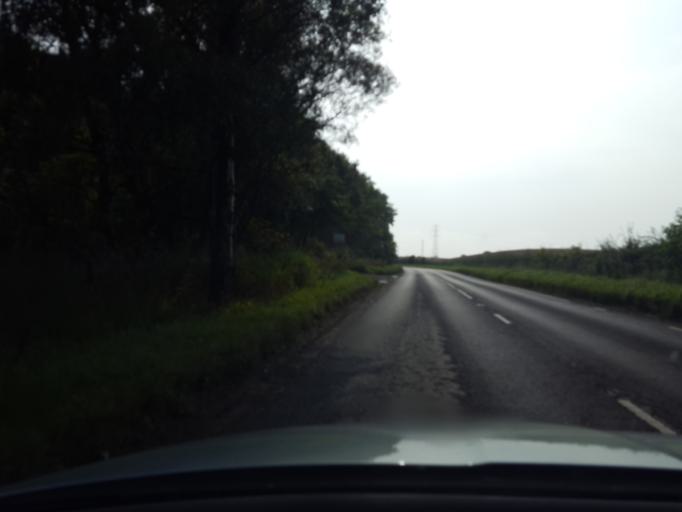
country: GB
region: Scotland
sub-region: Fife
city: Crossgates
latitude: 56.0617
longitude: -3.3813
